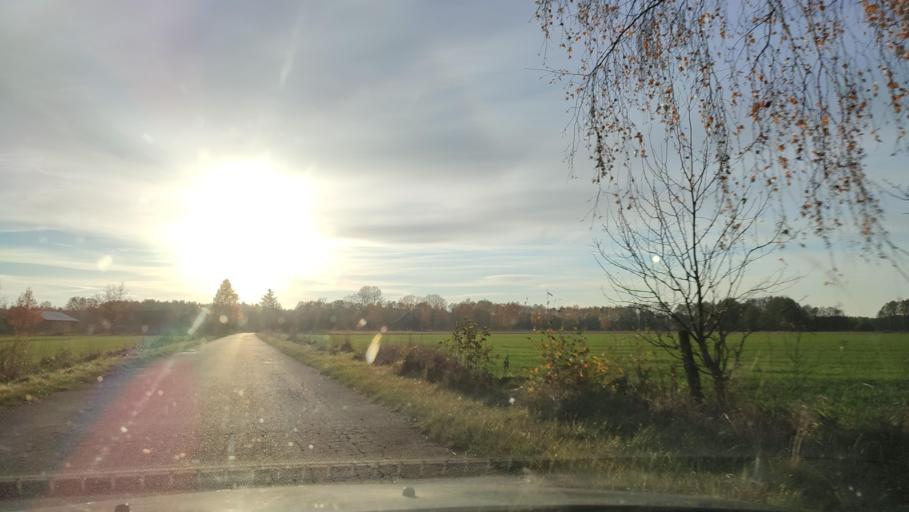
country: PL
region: Masovian Voivodeship
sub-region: Powiat mlawski
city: Dzierzgowo
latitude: 53.3307
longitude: 20.7043
